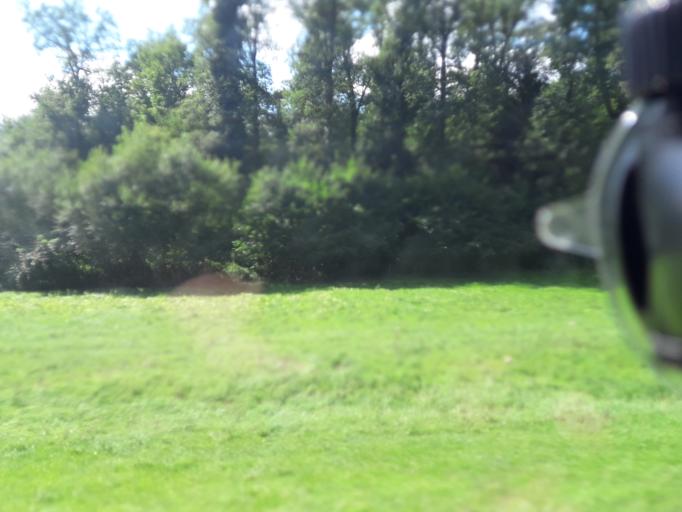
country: DE
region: North Rhine-Westphalia
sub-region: Regierungsbezirk Detmold
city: Paderborn
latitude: 51.6616
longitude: 8.7697
